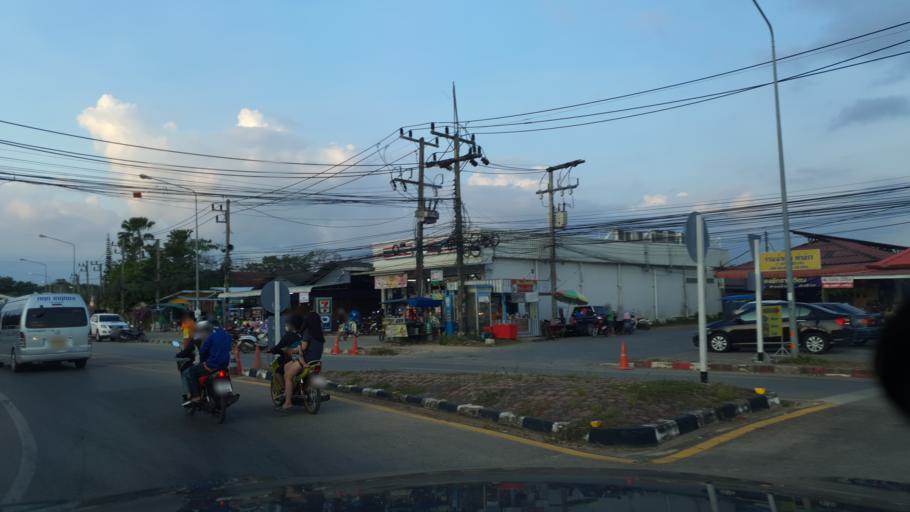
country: TH
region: Phangnga
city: Ban Ao Nang
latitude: 8.0329
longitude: 98.8617
